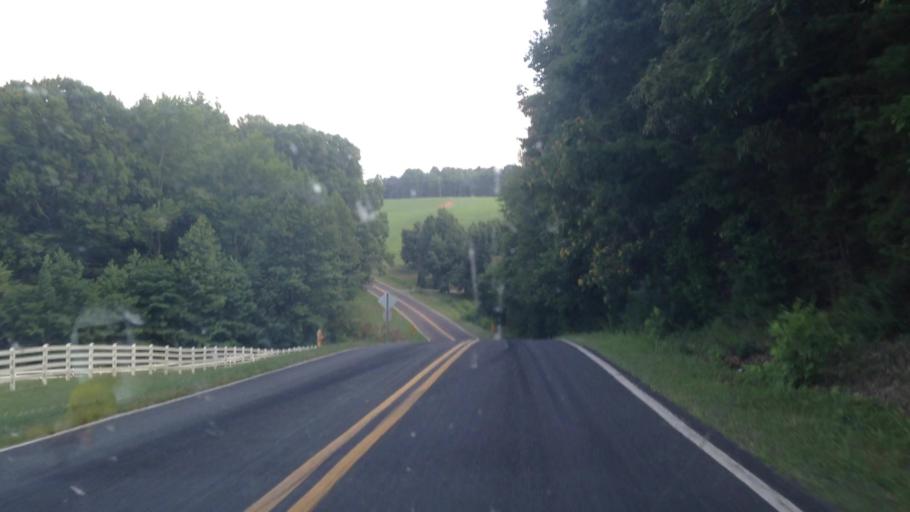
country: US
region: North Carolina
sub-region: Forsyth County
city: Walkertown
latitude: 36.1979
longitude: -80.1005
